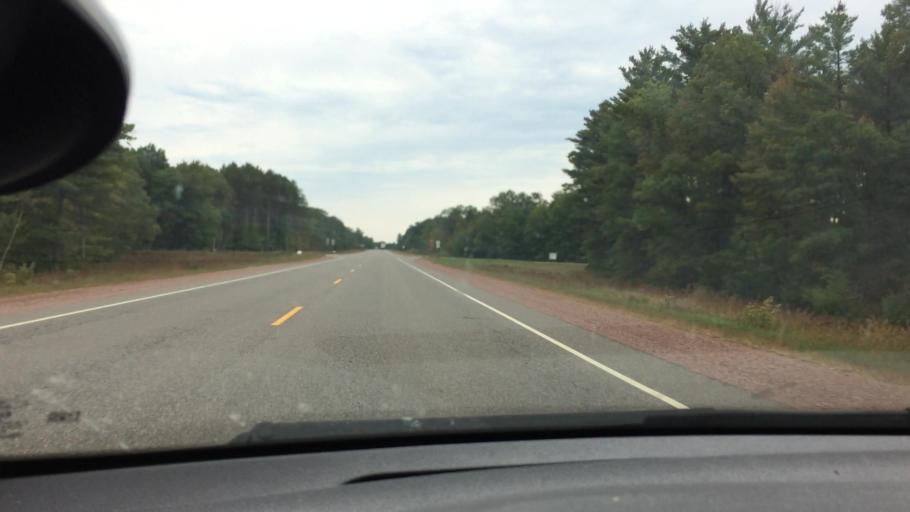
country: US
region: Wisconsin
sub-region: Clark County
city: Neillsville
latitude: 44.5657
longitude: -90.7087
